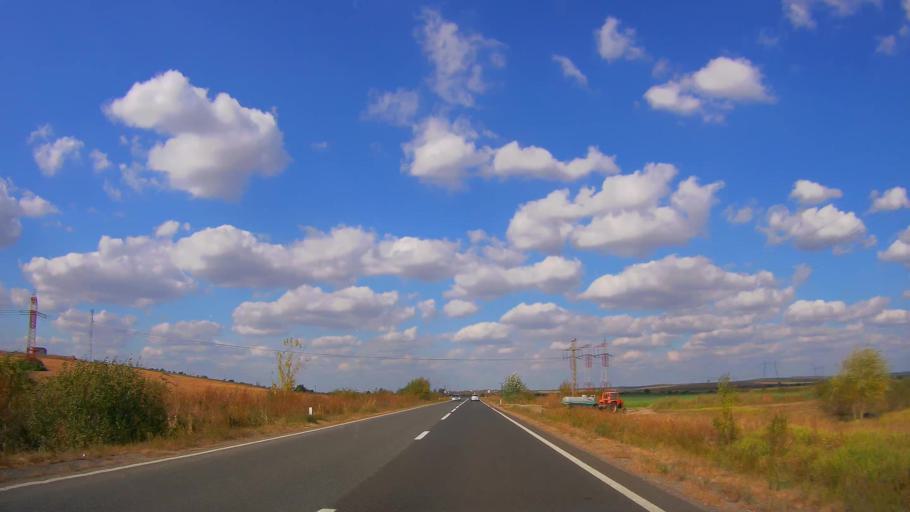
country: RO
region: Satu Mare
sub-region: Oras Ardud
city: Ardud
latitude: 47.6065
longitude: 22.8800
